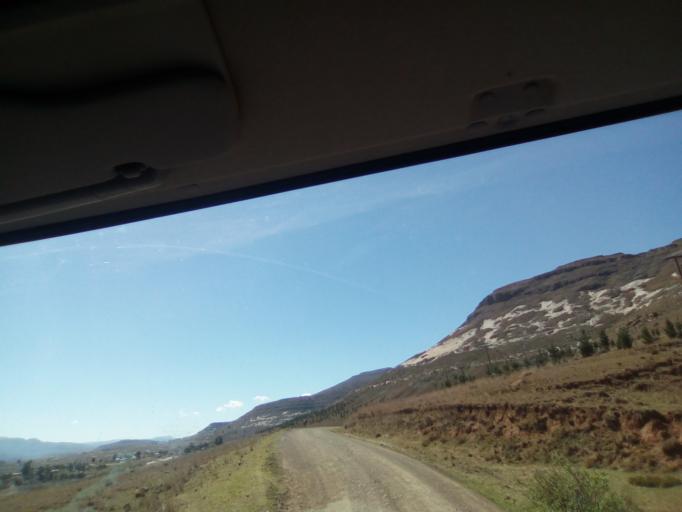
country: LS
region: Qacha's Nek
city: Qacha's Nek
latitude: -30.0361
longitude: 28.6721
